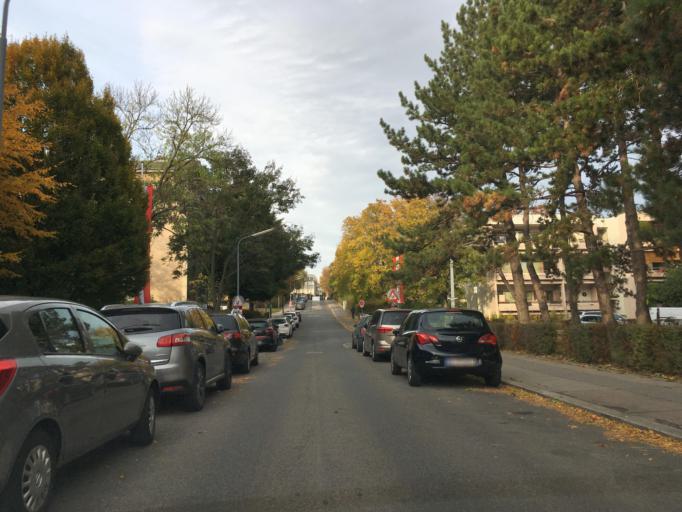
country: AT
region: Vienna
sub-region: Wien Stadt
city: Vienna
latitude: 48.2428
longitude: 16.3286
